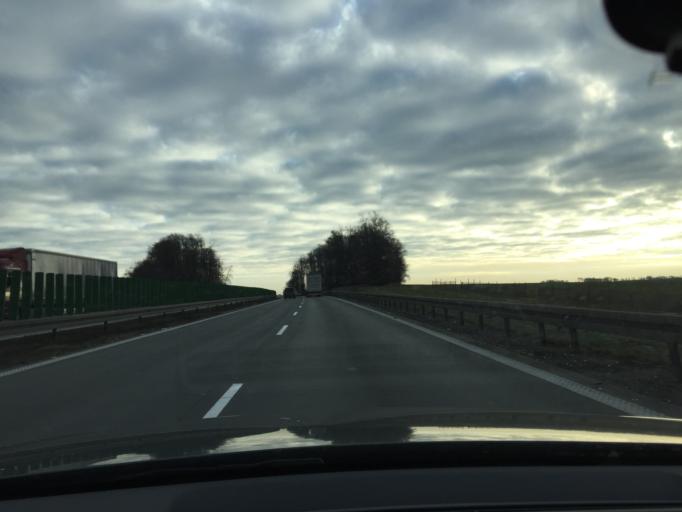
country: PL
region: Lower Silesian Voivodeship
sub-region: Powiat legnicki
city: Legnickie Pole
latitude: 51.1322
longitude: 16.3022
